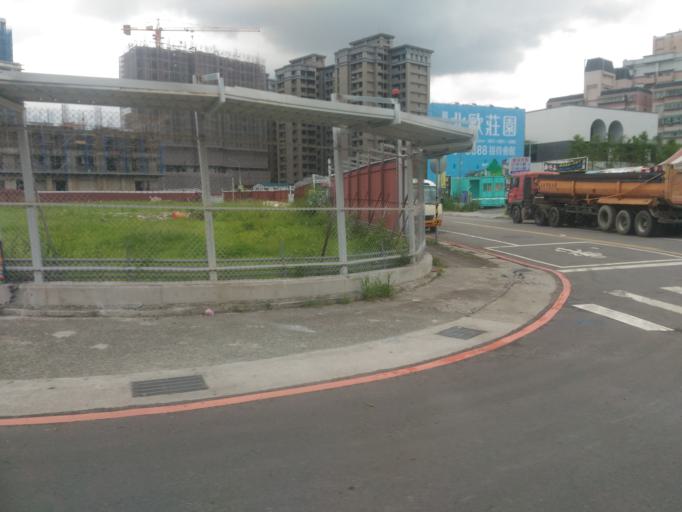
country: TW
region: Taipei
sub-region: Taipei
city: Banqiao
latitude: 25.0327
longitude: 121.4646
